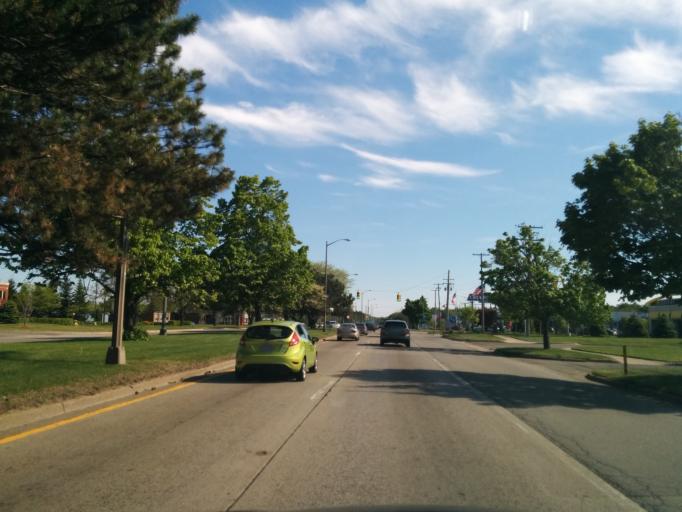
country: US
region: Michigan
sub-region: Ottawa County
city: Grand Haven
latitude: 43.0474
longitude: -86.2204
